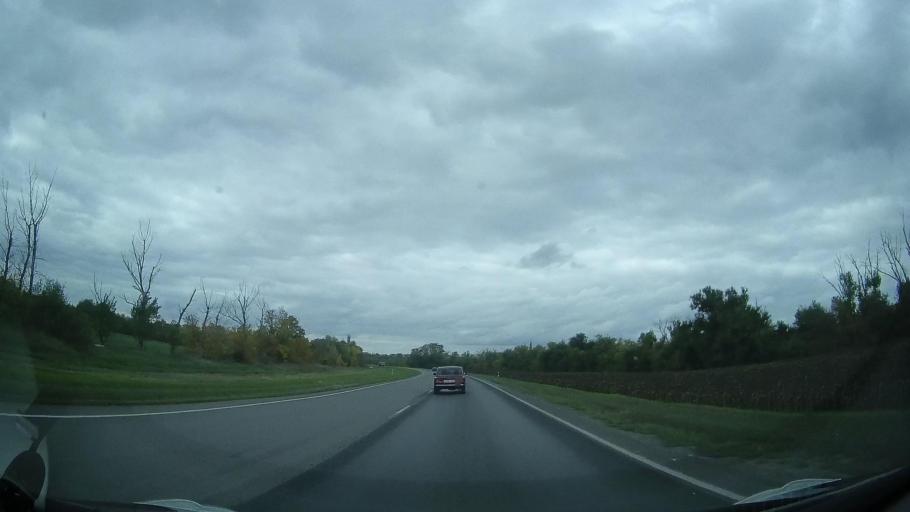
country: RU
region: Rostov
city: Yegorlykskaya
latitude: 46.5425
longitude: 40.7720
